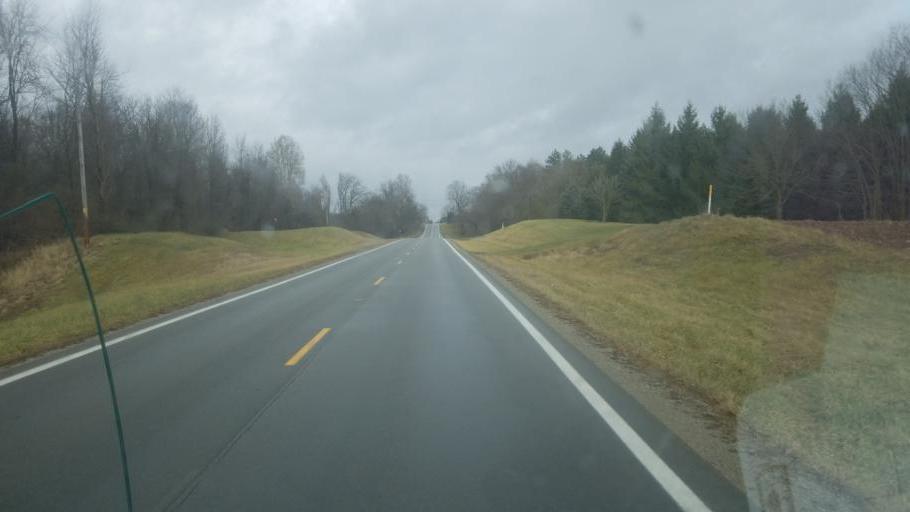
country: US
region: Ohio
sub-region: Crawford County
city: Bucyrus
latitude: 40.7695
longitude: -83.1308
